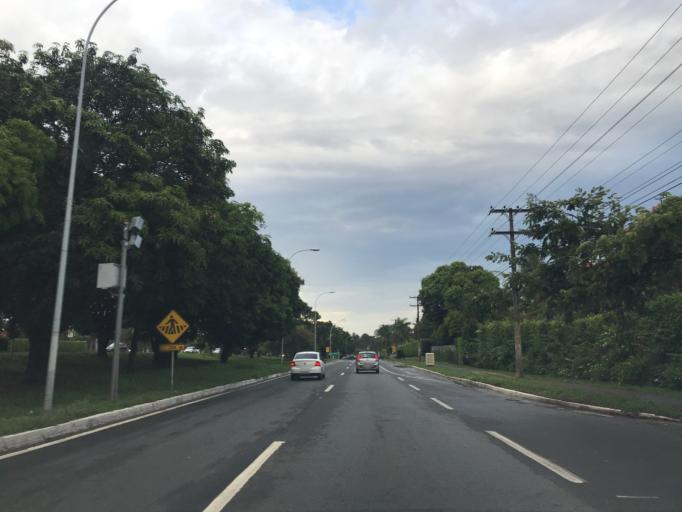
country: BR
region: Federal District
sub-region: Brasilia
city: Brasilia
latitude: -15.8427
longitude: -47.8702
